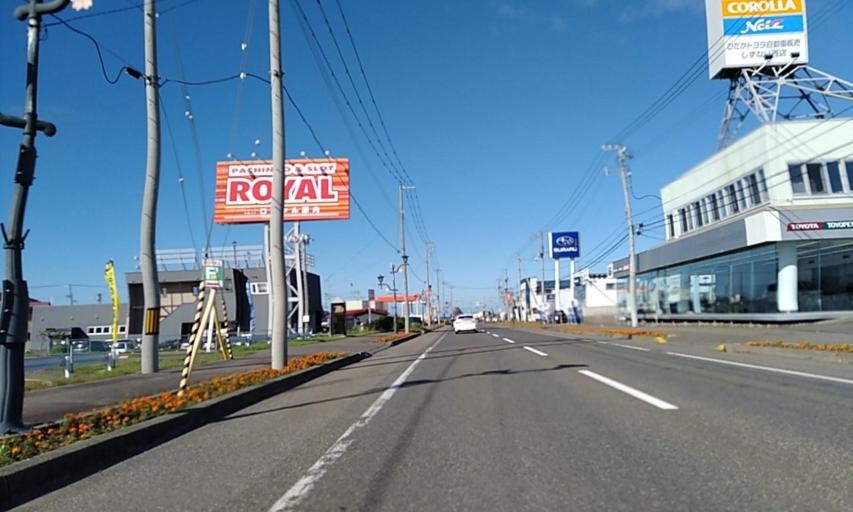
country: JP
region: Hokkaido
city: Shizunai-furukawacho
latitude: 42.3414
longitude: 142.3498
